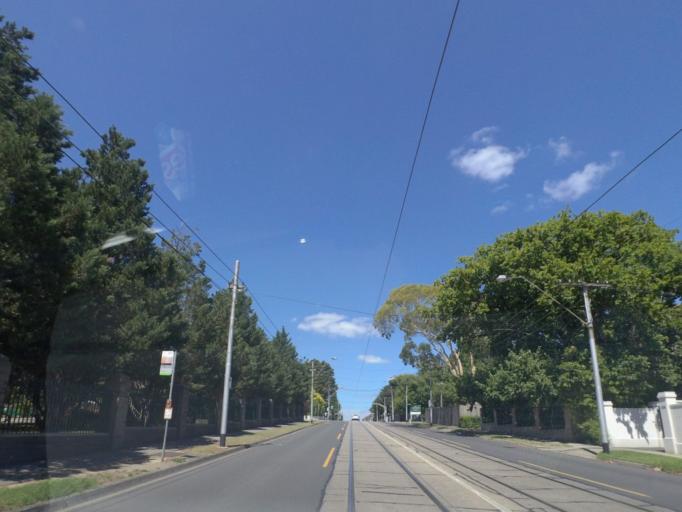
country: AU
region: Victoria
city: Balwyn
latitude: -37.8098
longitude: 145.0565
